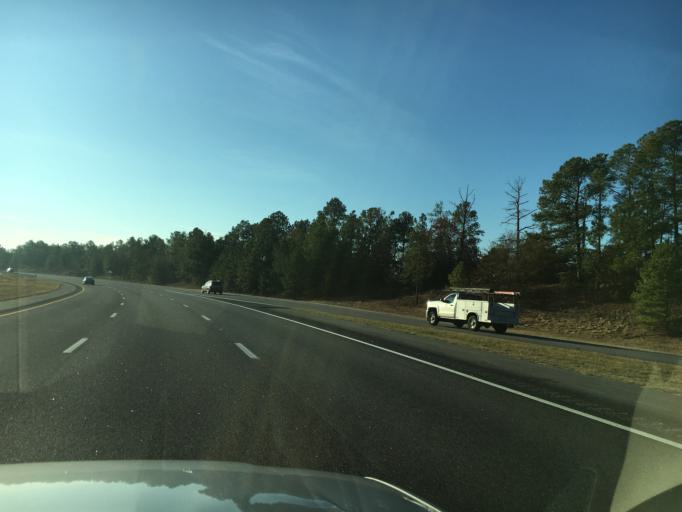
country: US
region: South Carolina
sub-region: Lexington County
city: Pineridge
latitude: 33.9228
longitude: -81.0684
